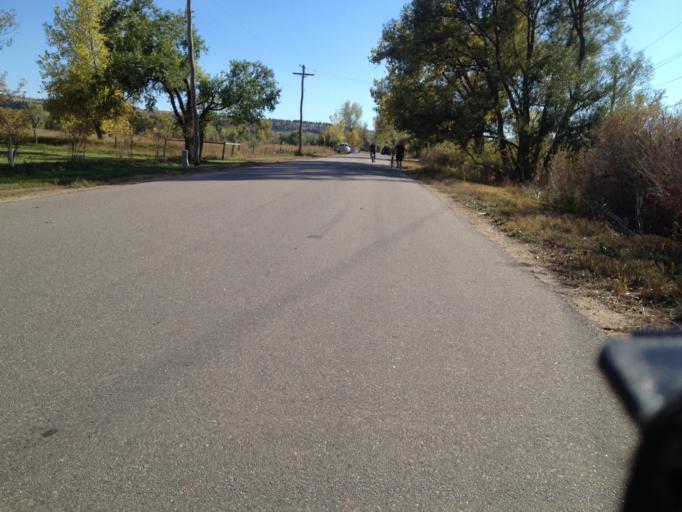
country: US
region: Colorado
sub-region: Boulder County
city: Boulder
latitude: 39.9694
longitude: -105.2366
